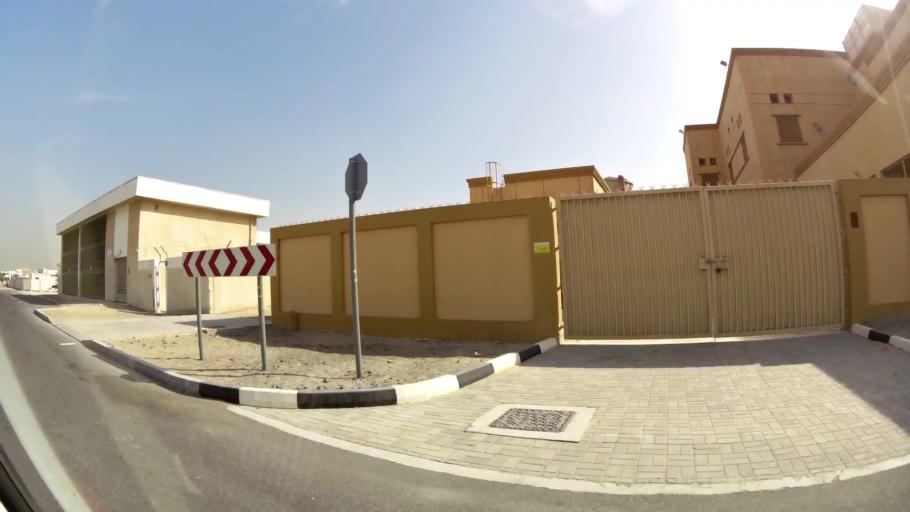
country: AE
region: Ash Shariqah
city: Sharjah
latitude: 25.2607
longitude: 55.3953
